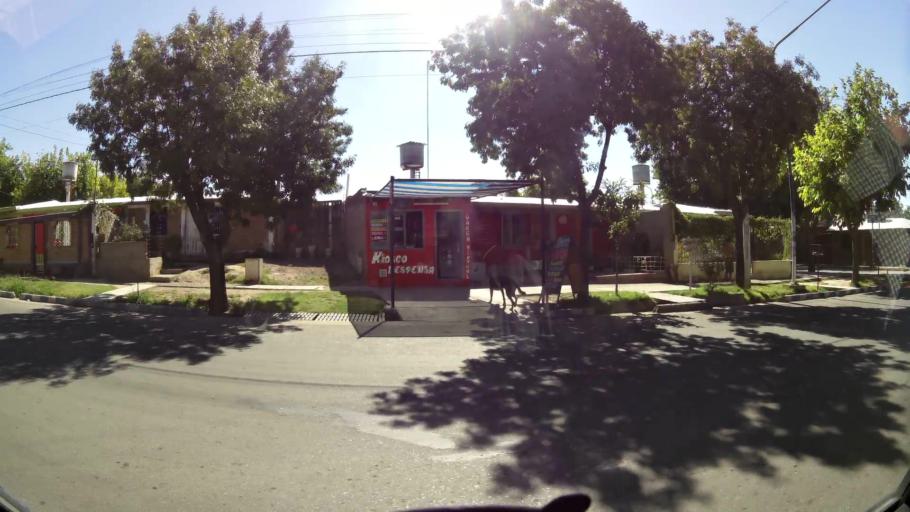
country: AR
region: Mendoza
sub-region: Departamento de Godoy Cruz
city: Godoy Cruz
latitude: -32.9519
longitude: -68.8219
